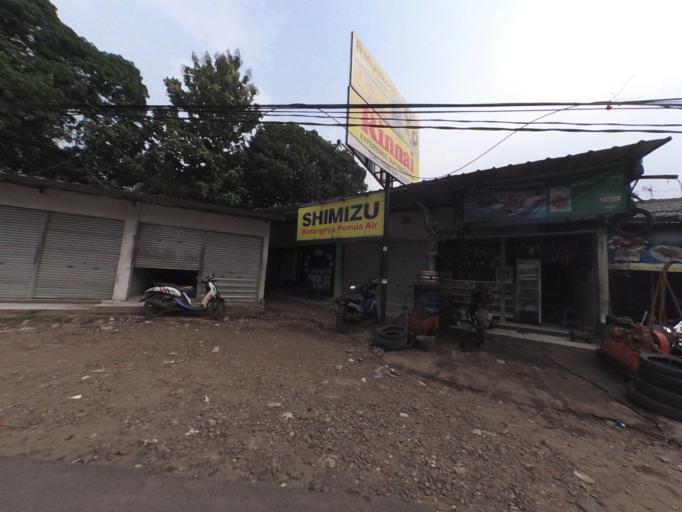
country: ID
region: West Java
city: Ciampea
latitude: -6.5564
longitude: 106.6953
